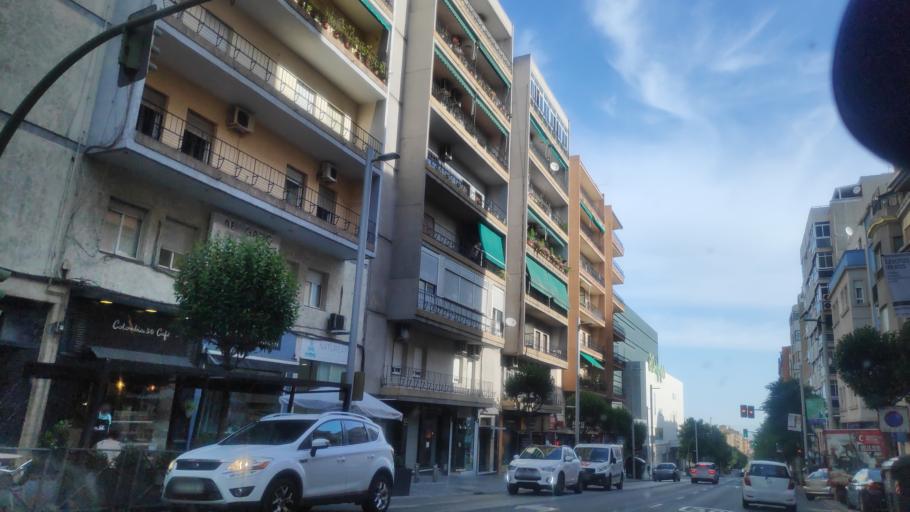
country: ES
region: Andalusia
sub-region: Provincia de Jaen
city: Jaen
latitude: 37.7738
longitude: -3.7857
